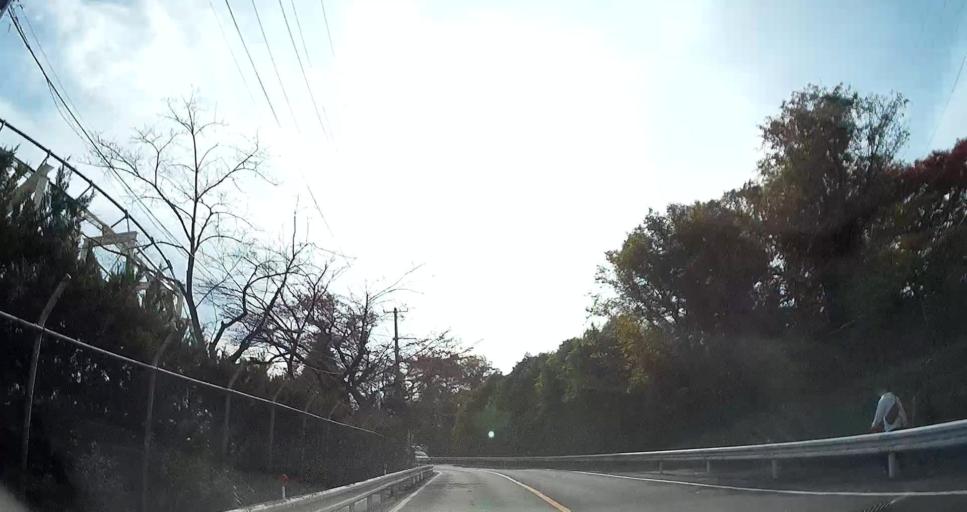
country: JP
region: Miyagi
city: Sendai
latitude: 38.2475
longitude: 140.8473
